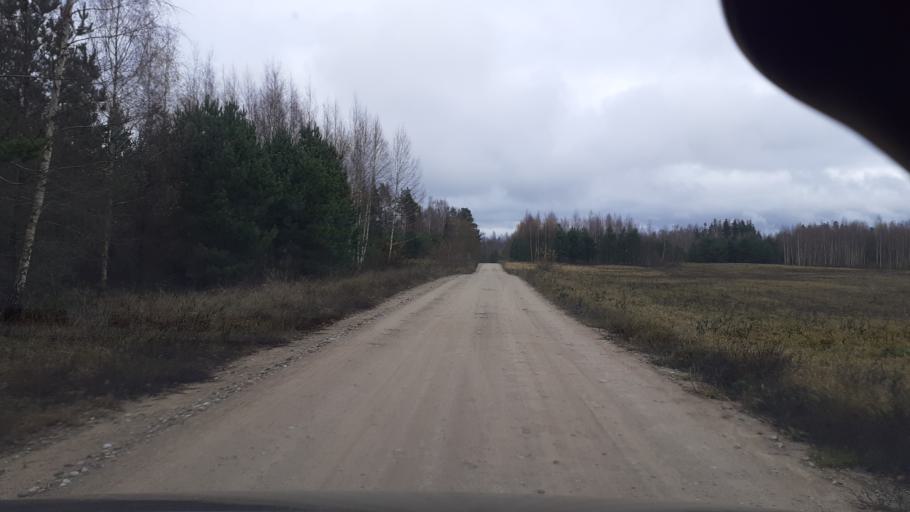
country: LV
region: Kuldigas Rajons
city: Kuldiga
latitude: 57.0343
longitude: 21.8775
